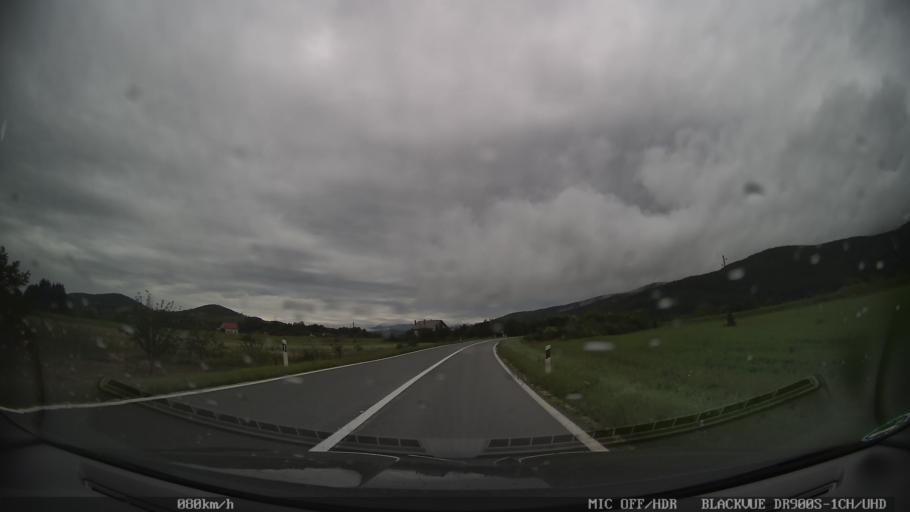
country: HR
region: Licko-Senjska
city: Brinje
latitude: 44.9477
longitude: 15.1259
